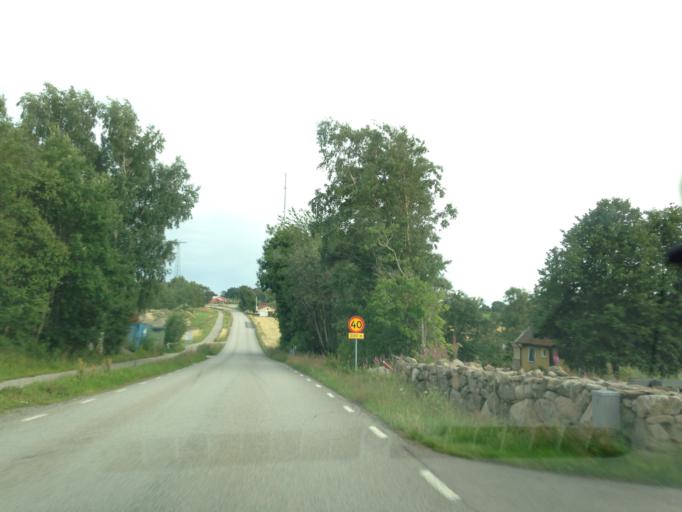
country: SE
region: Halland
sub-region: Varbergs Kommun
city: Tvaaker
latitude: 57.1195
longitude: 12.3914
